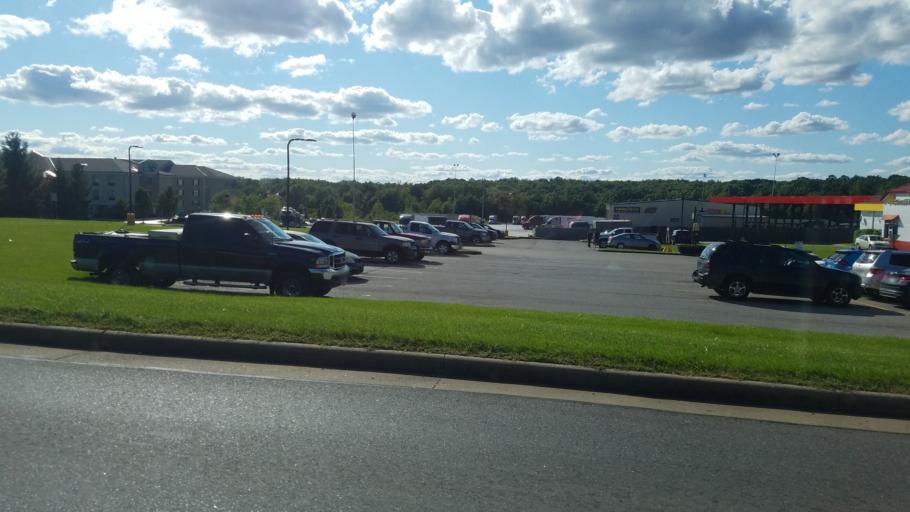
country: US
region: Ohio
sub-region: Trumbull County
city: Mineral Ridge
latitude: 41.1283
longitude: -80.7685
